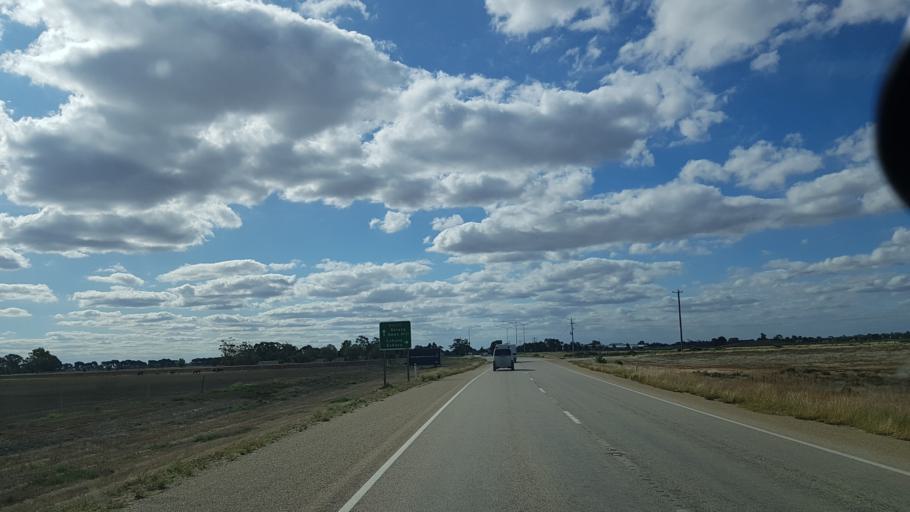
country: AU
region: Victoria
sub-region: Swan Hill
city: Swan Hill
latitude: -35.7655
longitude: 143.9322
